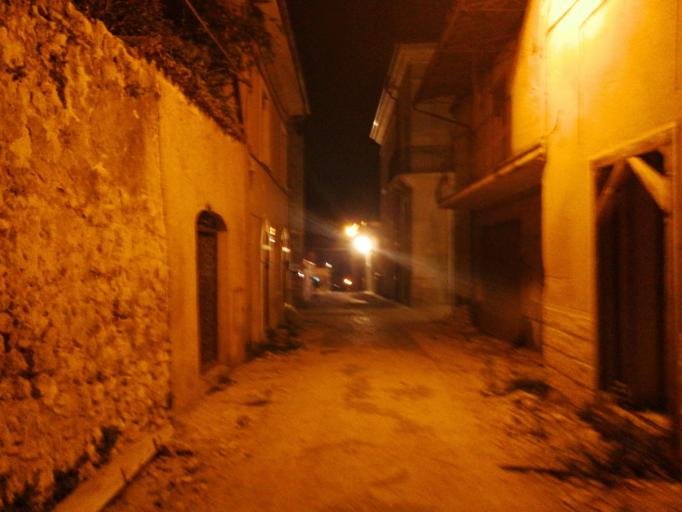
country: IT
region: Abruzzo
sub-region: Provincia dell' Aquila
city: L'Aquila
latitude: 42.3522
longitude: 13.3954
